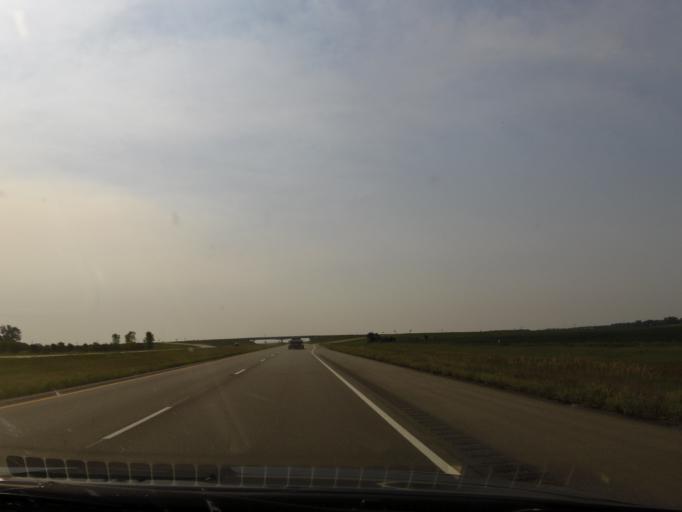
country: US
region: North Dakota
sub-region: Cass County
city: Horace
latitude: 46.6354
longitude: -96.8320
